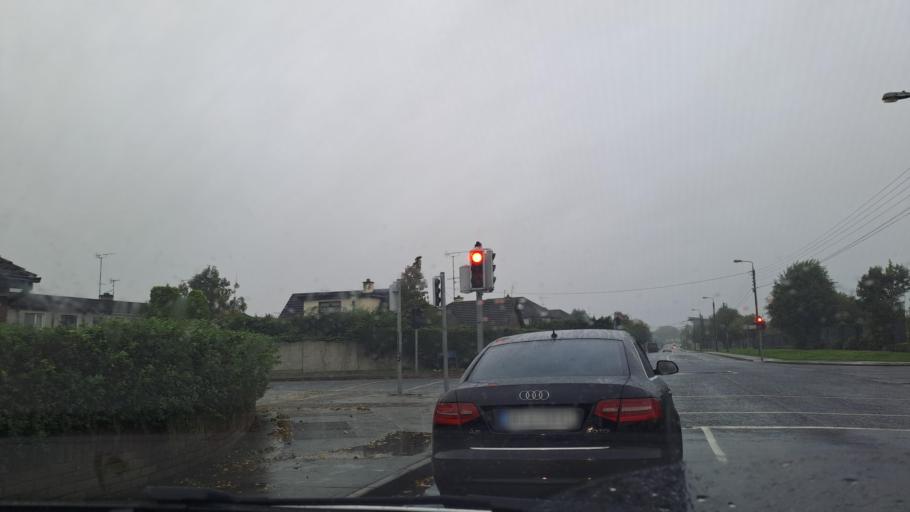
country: IE
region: Leinster
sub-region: Lu
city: Dundalk
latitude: 53.9958
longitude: -6.3983
